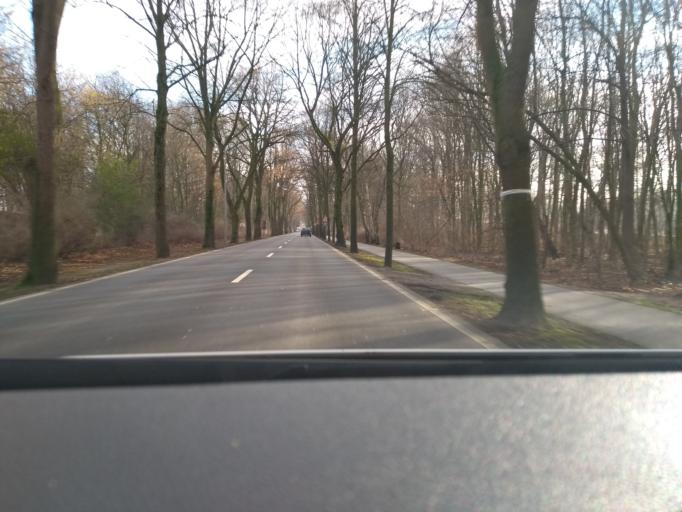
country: DE
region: North Rhine-Westphalia
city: Lunen
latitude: 51.6154
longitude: 7.4924
